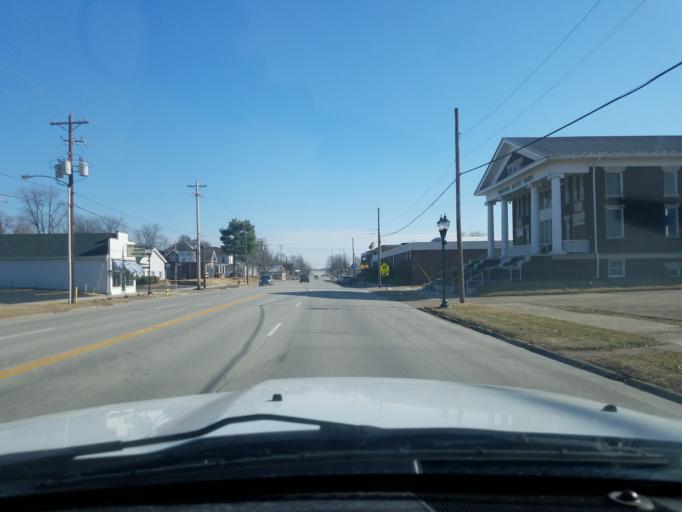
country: US
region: Kentucky
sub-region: Henderson County
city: Henderson
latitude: 37.8386
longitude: -87.5863
